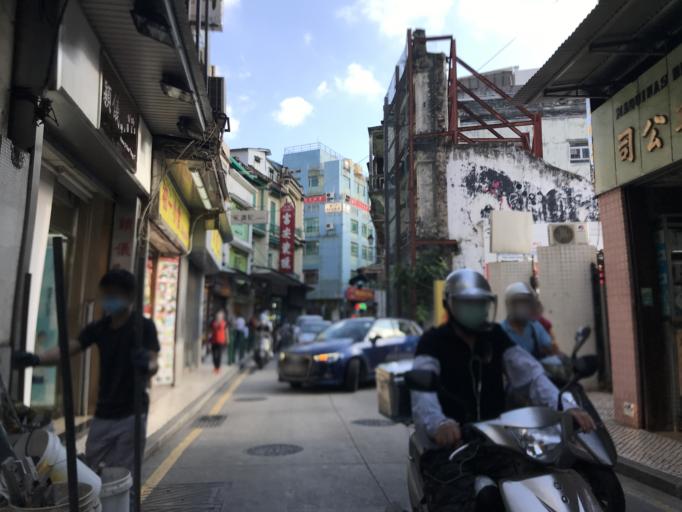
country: MO
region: Macau
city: Macau
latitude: 22.1953
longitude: 113.5400
